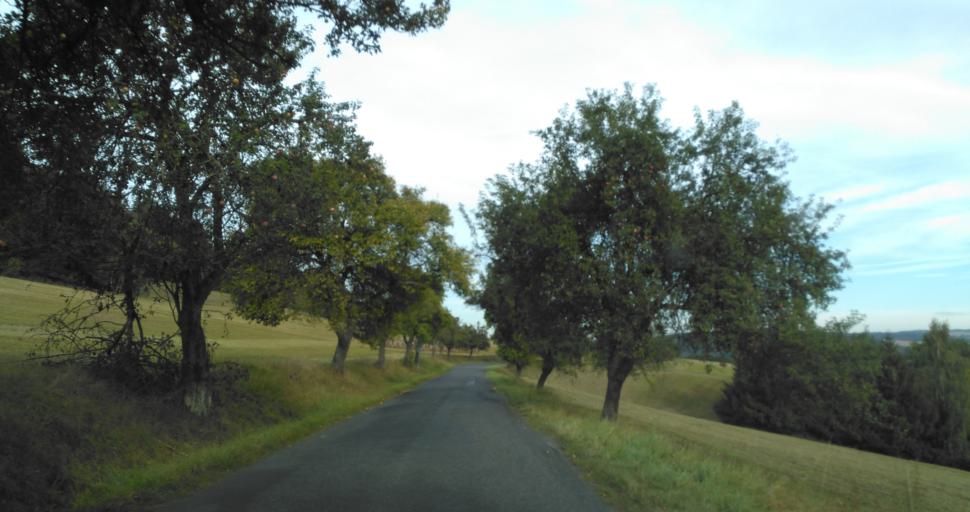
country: CZ
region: Plzensky
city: Zbiroh
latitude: 49.9540
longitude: 13.7765
